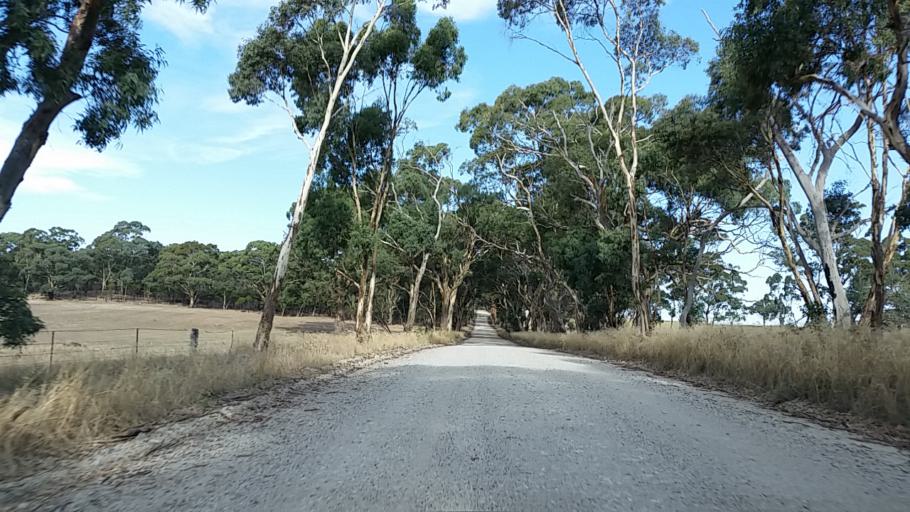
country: AU
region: South Australia
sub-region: Barossa
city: Angaston
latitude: -34.5756
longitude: 139.1296
